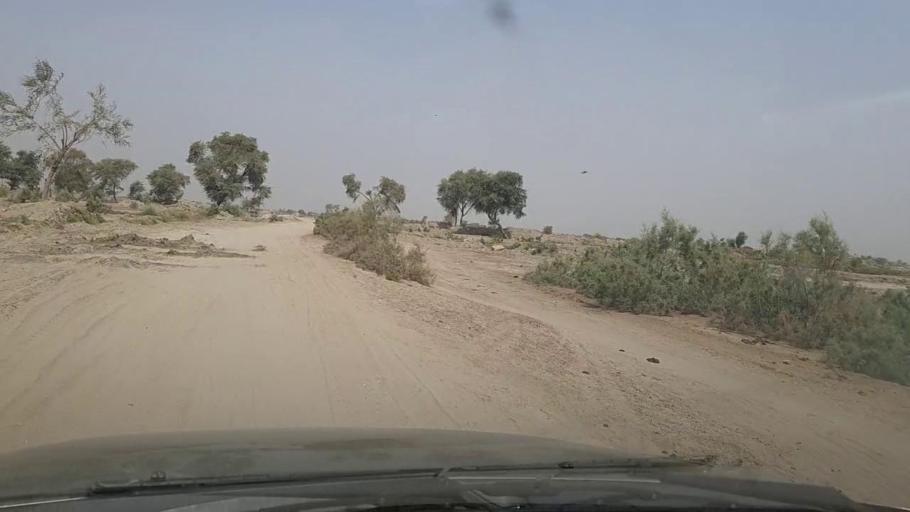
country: PK
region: Sindh
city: Thul
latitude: 28.4029
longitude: 68.7055
